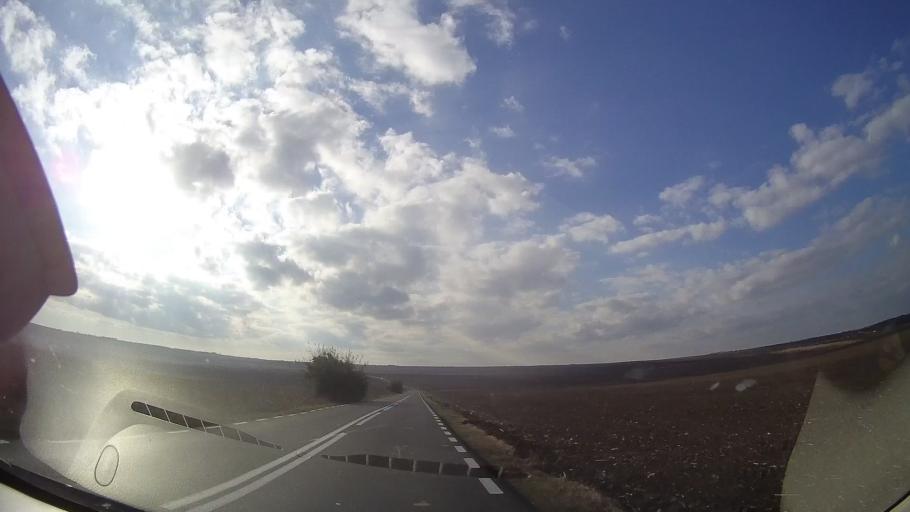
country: RO
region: Constanta
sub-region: Comuna Limanu
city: Limanu
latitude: 43.8226
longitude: 28.4787
